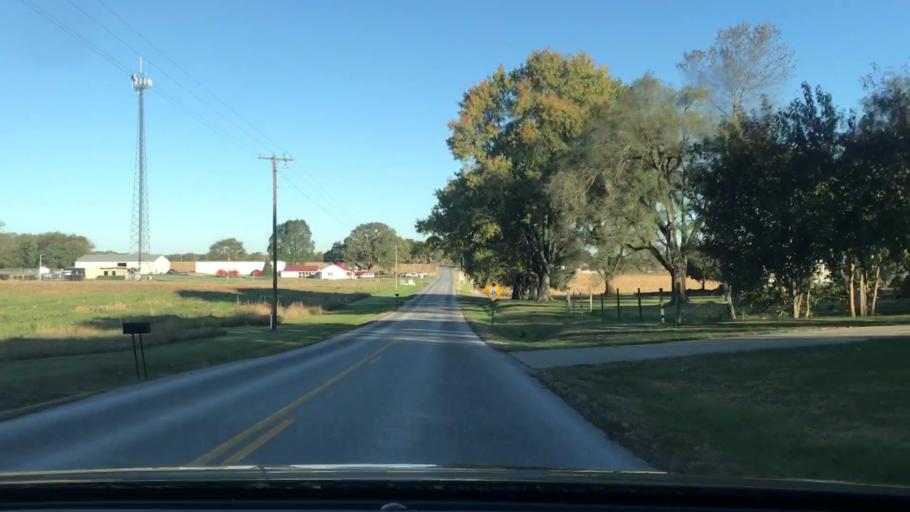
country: US
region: Kentucky
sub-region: Logan County
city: Auburn
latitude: 36.8493
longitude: -86.7050
